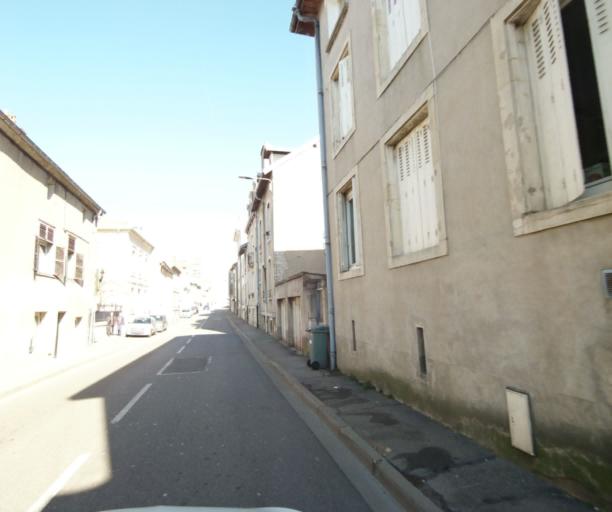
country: FR
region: Lorraine
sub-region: Departement de Meurthe-et-Moselle
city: Malzeville
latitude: 48.7094
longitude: 6.1846
